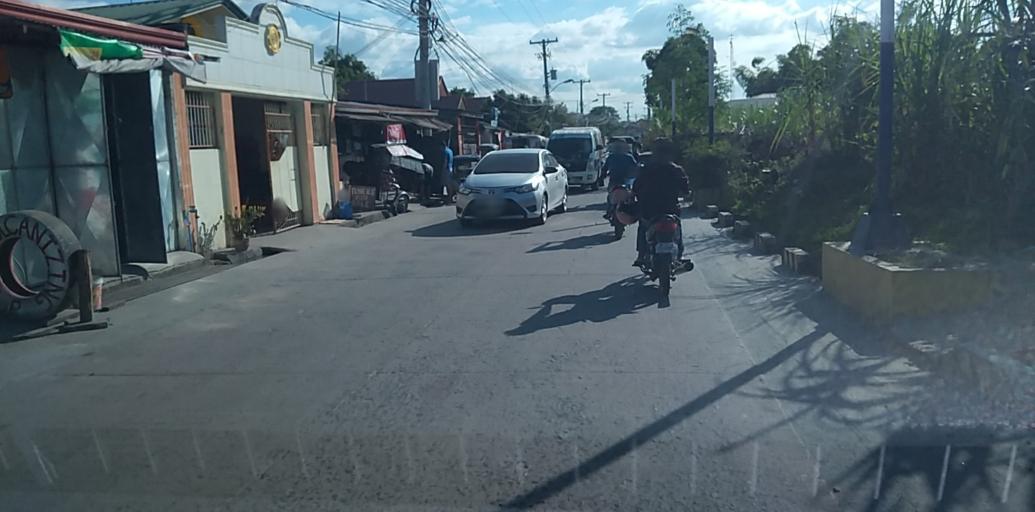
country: PH
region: Central Luzon
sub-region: Province of Pampanga
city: Acli
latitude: 15.1158
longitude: 120.6341
